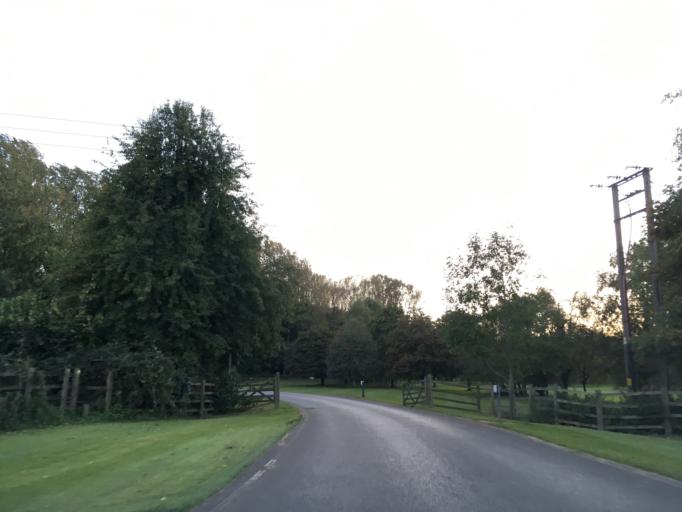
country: GB
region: England
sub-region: South Gloucestershire
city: Thornbury
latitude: 51.6016
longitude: -2.5285
